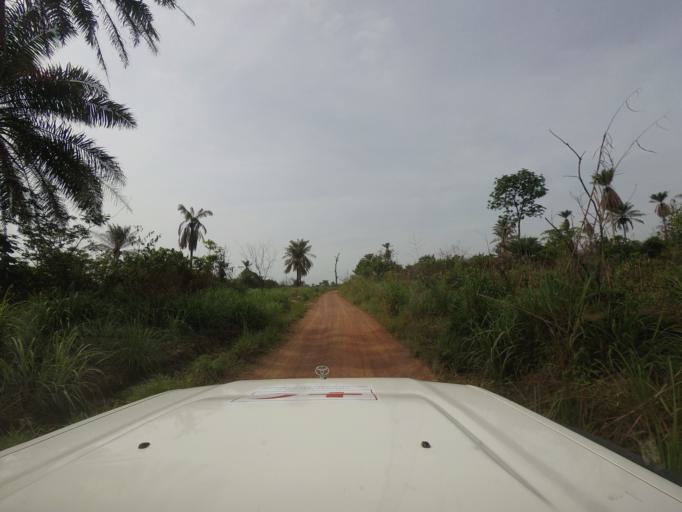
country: GN
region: Nzerekore
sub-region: Macenta
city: Macenta
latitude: 8.5053
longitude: -9.5305
